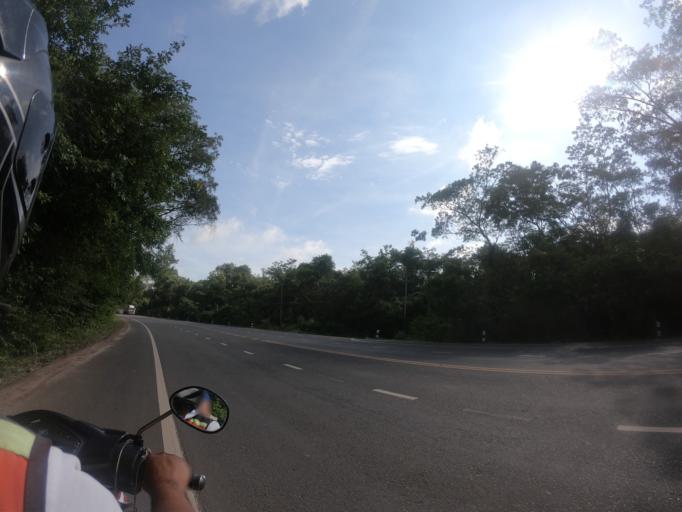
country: TH
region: Surin
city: Kap Choeng
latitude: 14.4478
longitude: 103.7006
